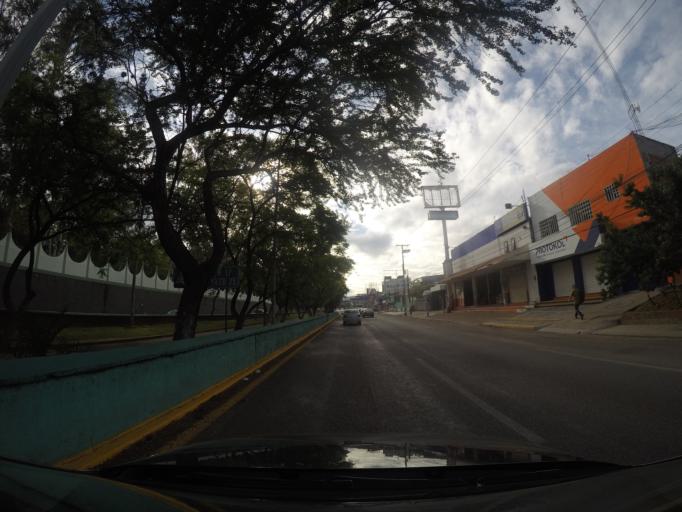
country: MX
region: Oaxaca
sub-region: Santa Cruz Amilpas
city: Santa Cruz Amilpas
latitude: 17.0691
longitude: -96.6988
